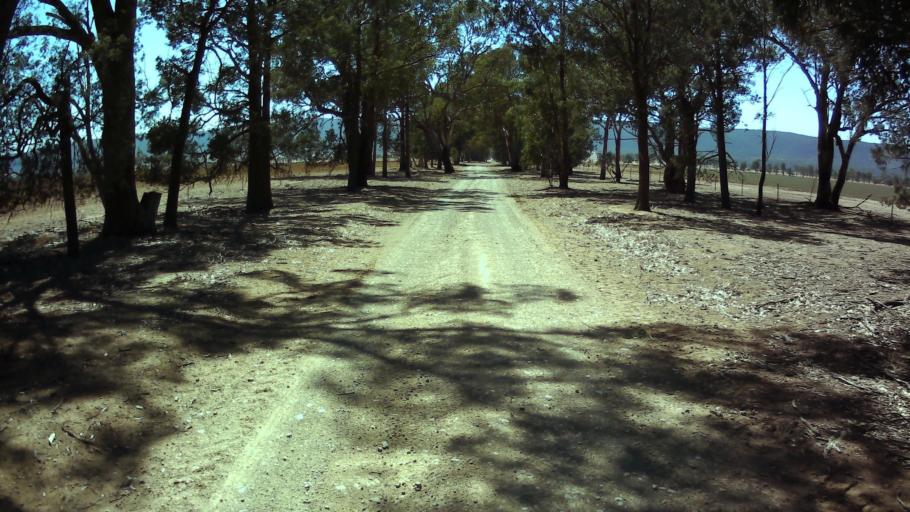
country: AU
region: New South Wales
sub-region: Weddin
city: Grenfell
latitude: -33.7003
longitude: 148.3093
